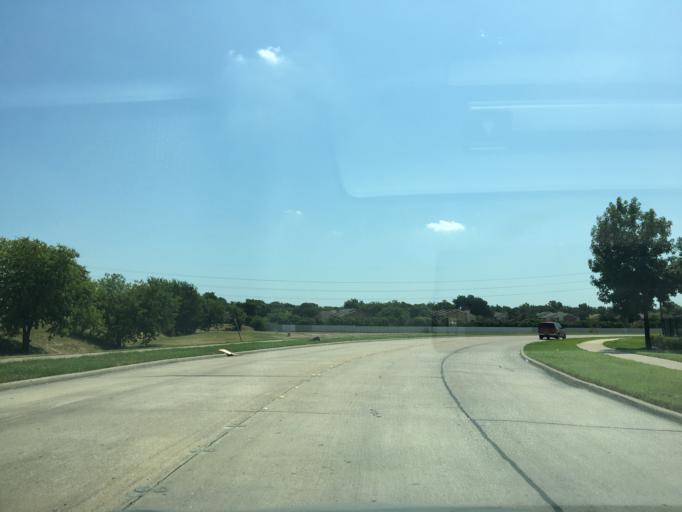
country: US
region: Texas
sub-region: Dallas County
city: Garland
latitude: 32.8692
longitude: -96.6617
